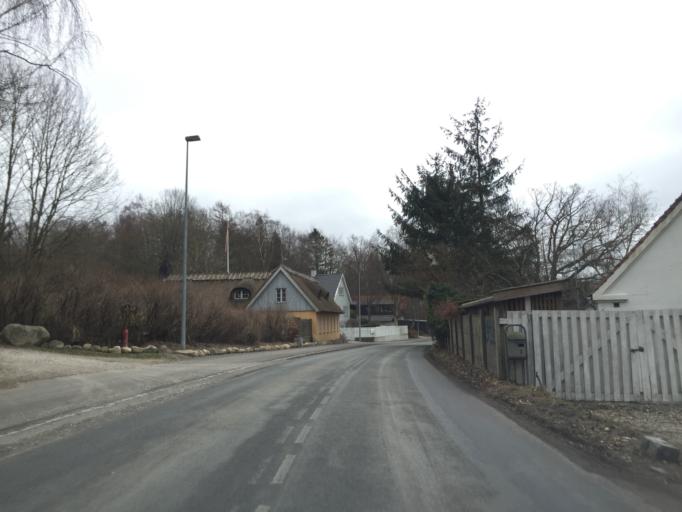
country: DK
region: Capital Region
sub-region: Hillerod Kommune
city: Hillerod
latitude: 55.9118
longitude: 12.3272
